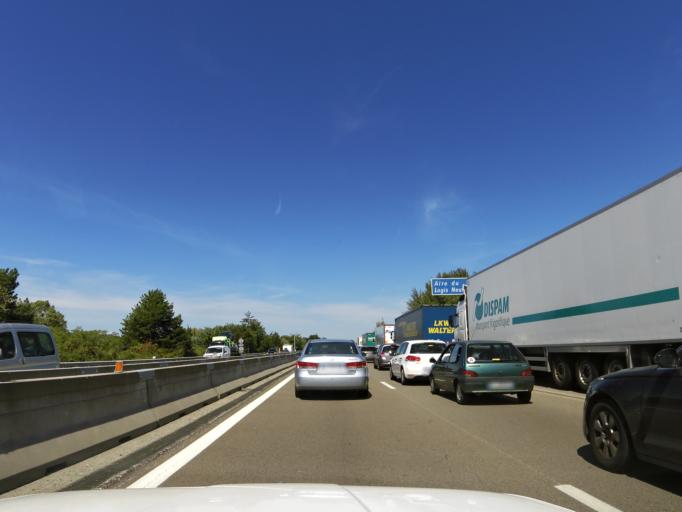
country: FR
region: Rhone-Alpes
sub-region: Departement de l'Ardeche
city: Cruas
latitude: 44.6399
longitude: 4.7918
